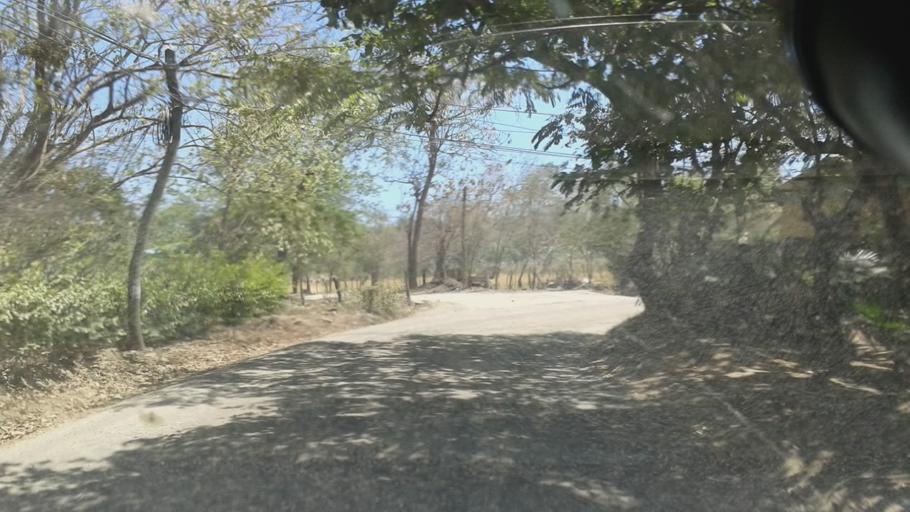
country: CR
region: Guanacaste
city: Samara
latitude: 9.9727
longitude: -85.6631
